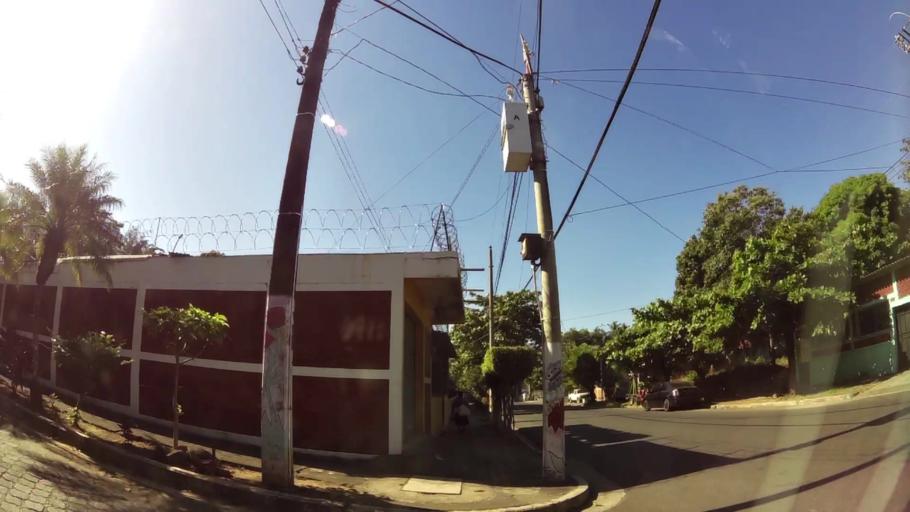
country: SV
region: Sonsonate
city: Sonzacate
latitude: 13.7298
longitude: -89.7209
